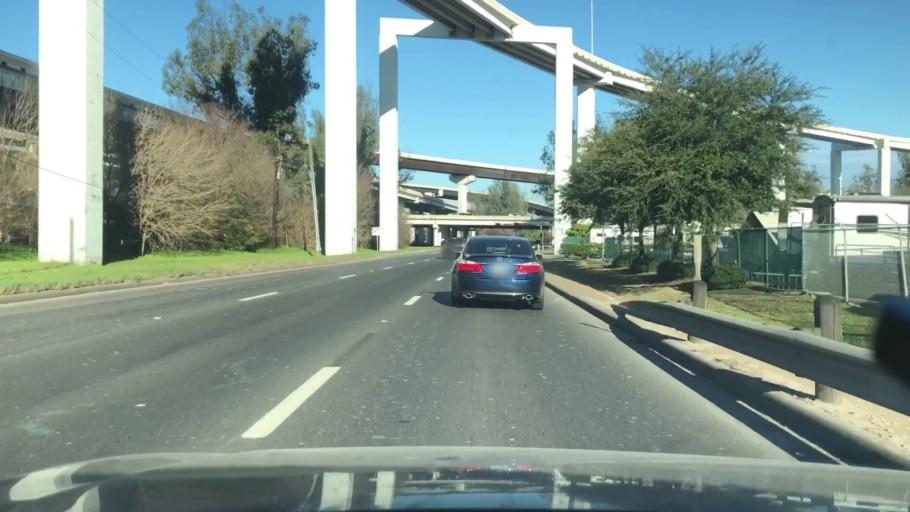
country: US
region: Texas
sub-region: Fort Bend County
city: Meadows Place
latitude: 29.6595
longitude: -95.5561
